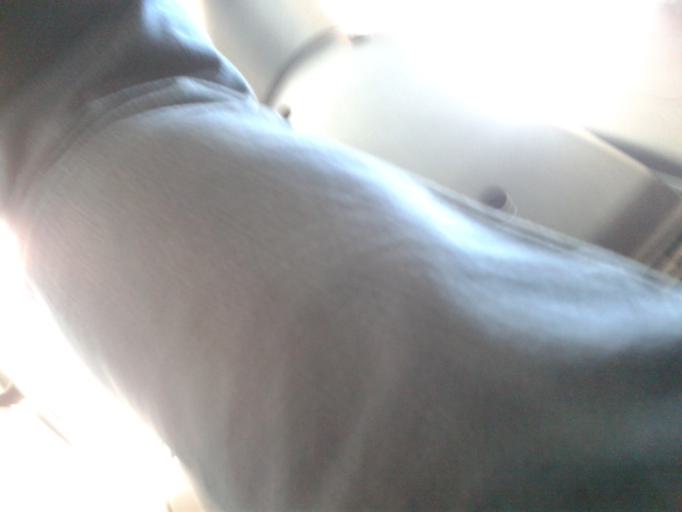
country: BR
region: Minas Gerais
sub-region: Ituiutaba
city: Ituiutaba
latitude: -19.0840
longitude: -49.7402
